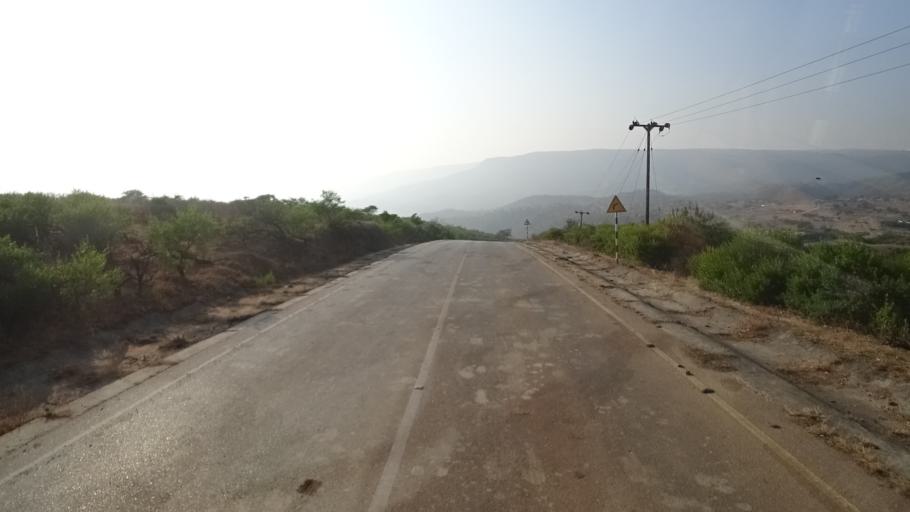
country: YE
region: Al Mahrah
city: Hawf
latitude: 16.7461
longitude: 53.3457
